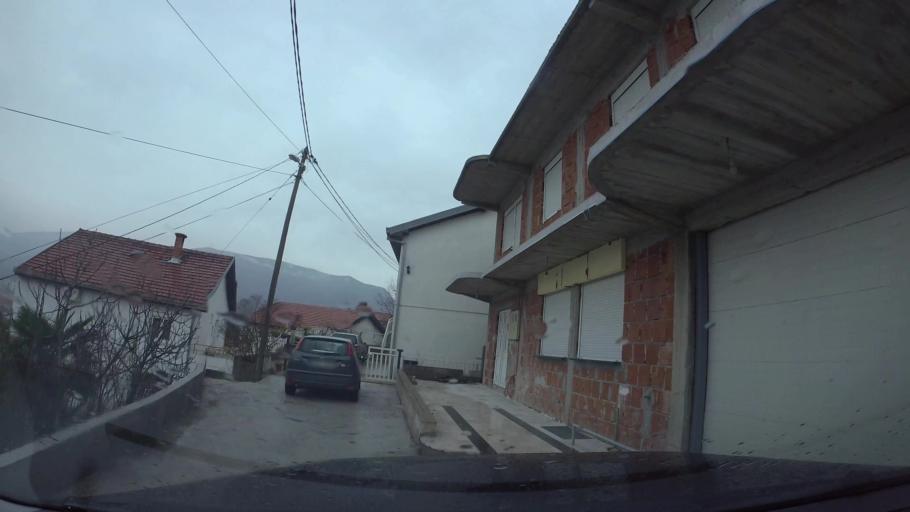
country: BA
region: Federation of Bosnia and Herzegovina
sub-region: Hercegovacko-Bosanski Kanton
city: Mostar
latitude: 43.3438
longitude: 17.8181
